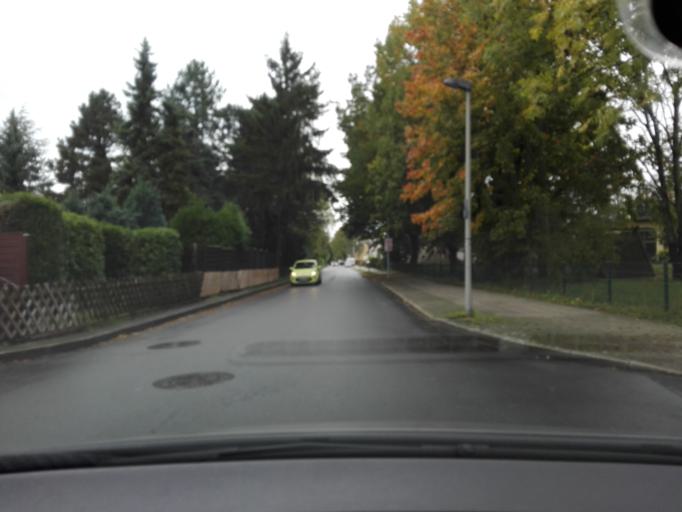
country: DE
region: North Rhine-Westphalia
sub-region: Regierungsbezirk Arnsberg
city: Unna
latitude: 51.5591
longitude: 7.6880
